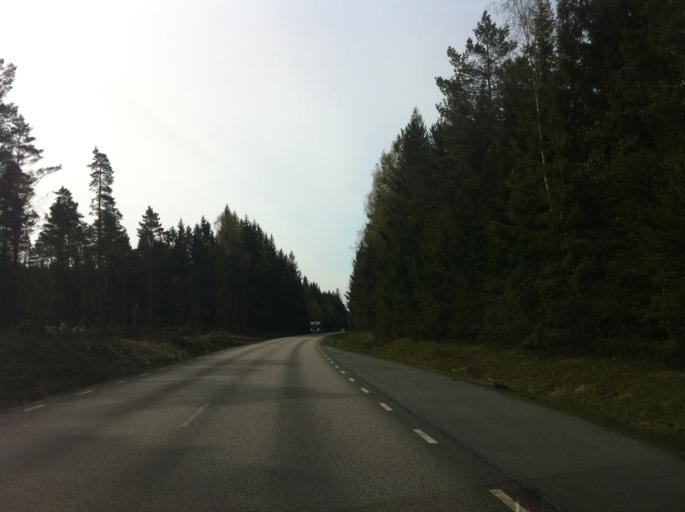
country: SE
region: Vaestra Goetaland
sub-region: Marks Kommun
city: Kinna
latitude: 57.4157
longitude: 12.7742
